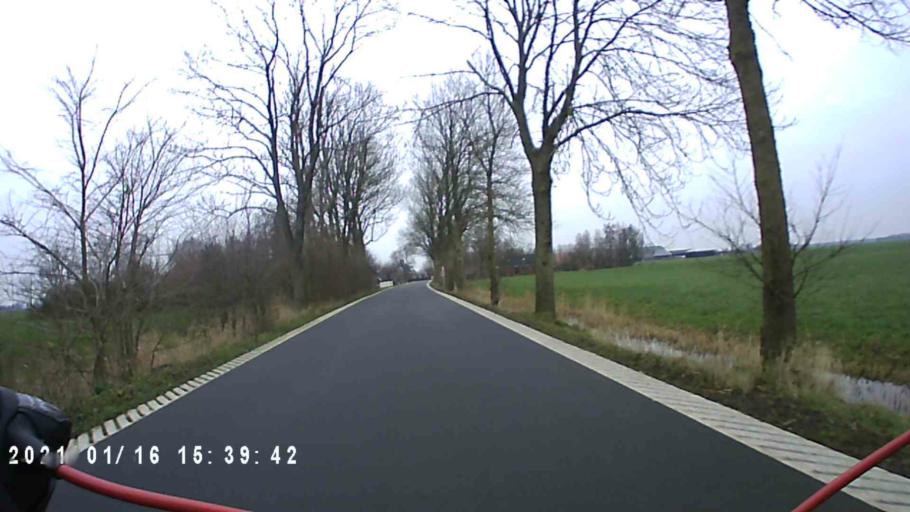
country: NL
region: Groningen
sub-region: Gemeente Groningen
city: Korrewegwijk
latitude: 53.2684
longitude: 6.5652
